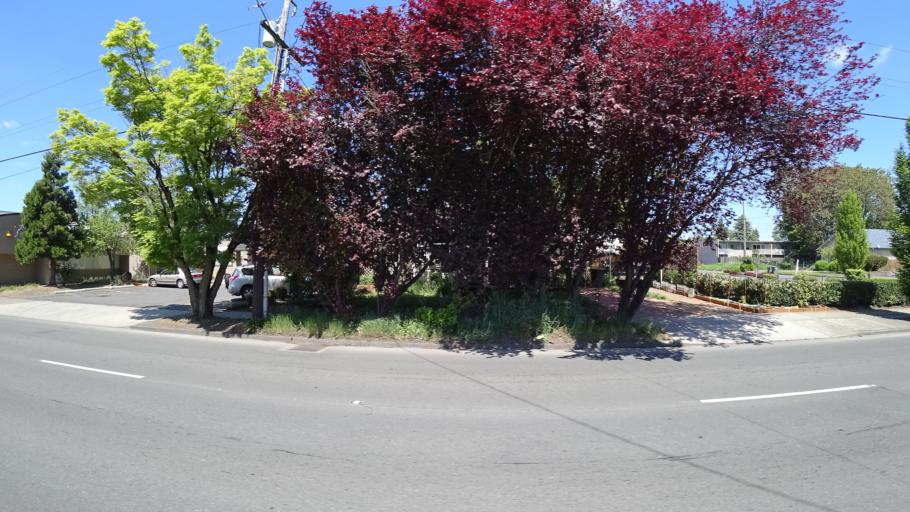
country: US
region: Oregon
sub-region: Washington County
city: Hillsboro
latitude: 45.5188
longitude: -122.9849
